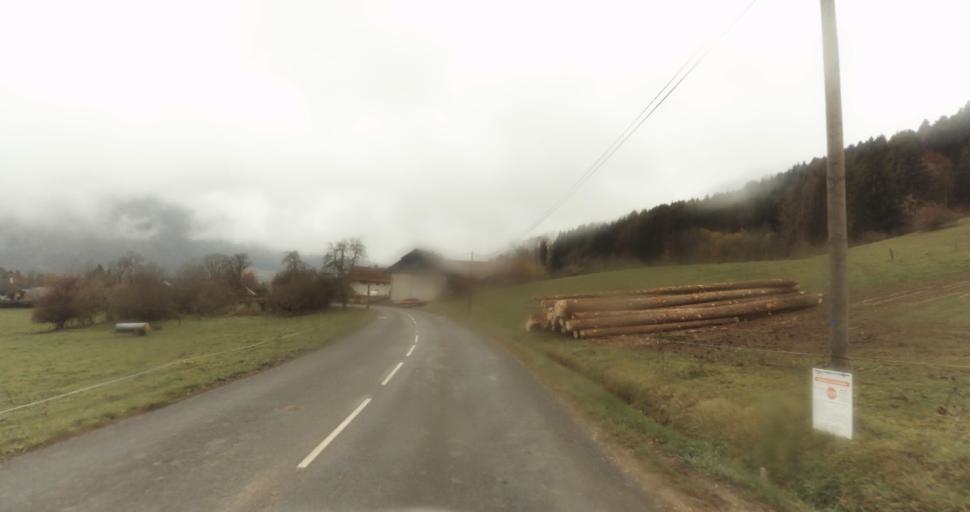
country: FR
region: Rhone-Alpes
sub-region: Departement de la Haute-Savoie
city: Thorens-Glieres
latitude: 46.0071
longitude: 6.2591
